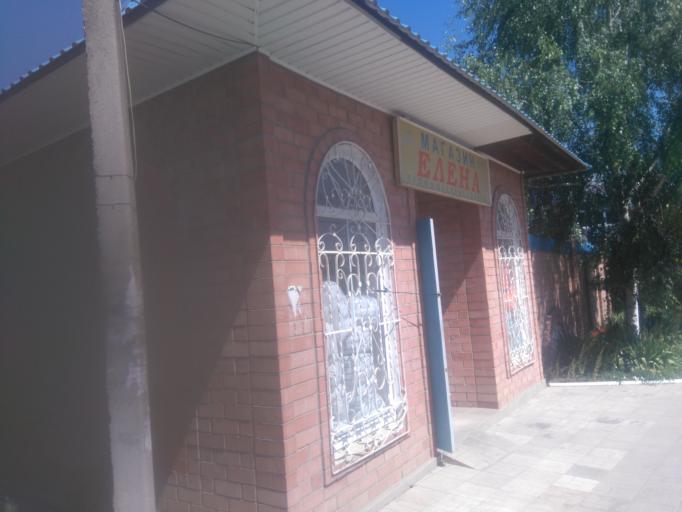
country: RU
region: Krasnodarskiy
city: Fastovetskaya
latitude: 45.9175
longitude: 40.1548
